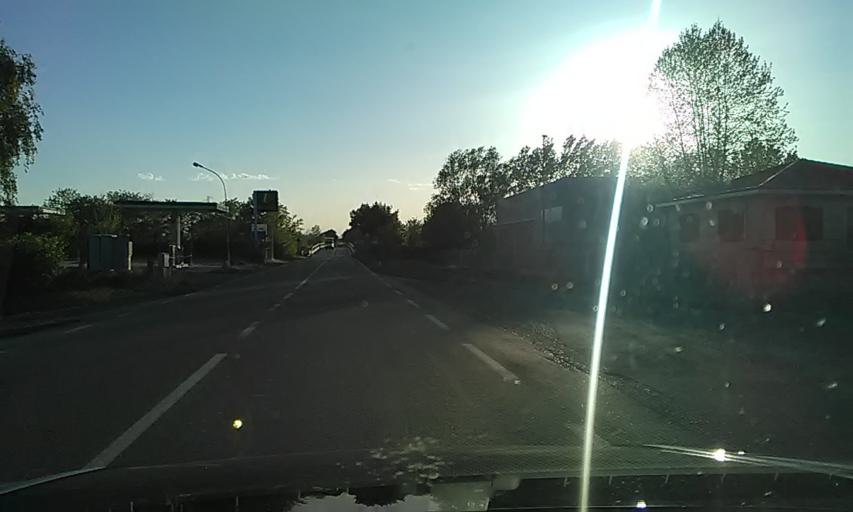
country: IT
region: Piedmont
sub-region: Provincia di Vercelli
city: Ghislarengo
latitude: 45.5307
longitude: 8.4000
